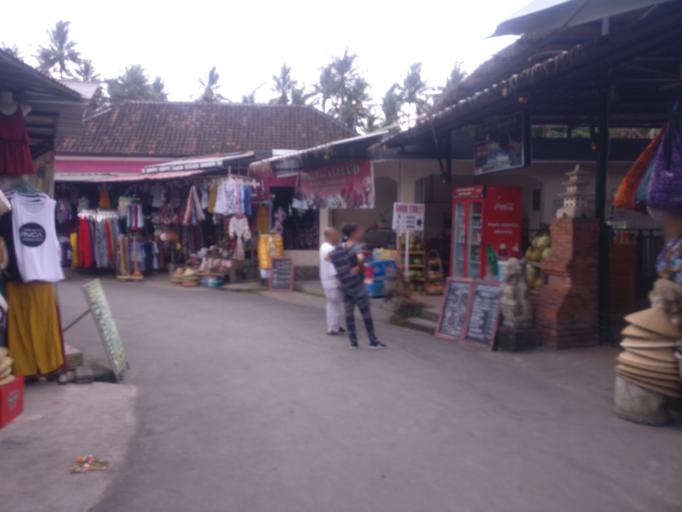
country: ID
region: Bali
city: Banjar Desa
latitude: -8.5756
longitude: 115.2889
